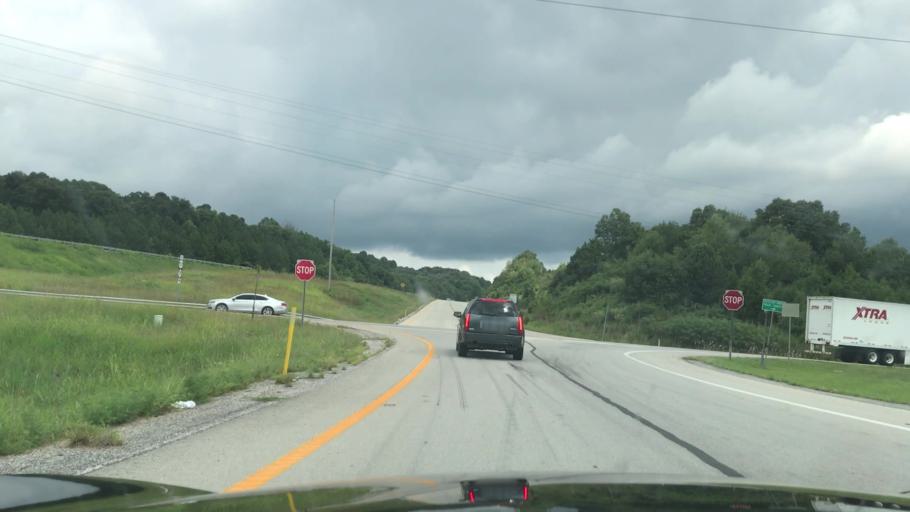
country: US
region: Kentucky
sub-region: Butler County
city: Morgantown
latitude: 37.2153
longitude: -86.7100
